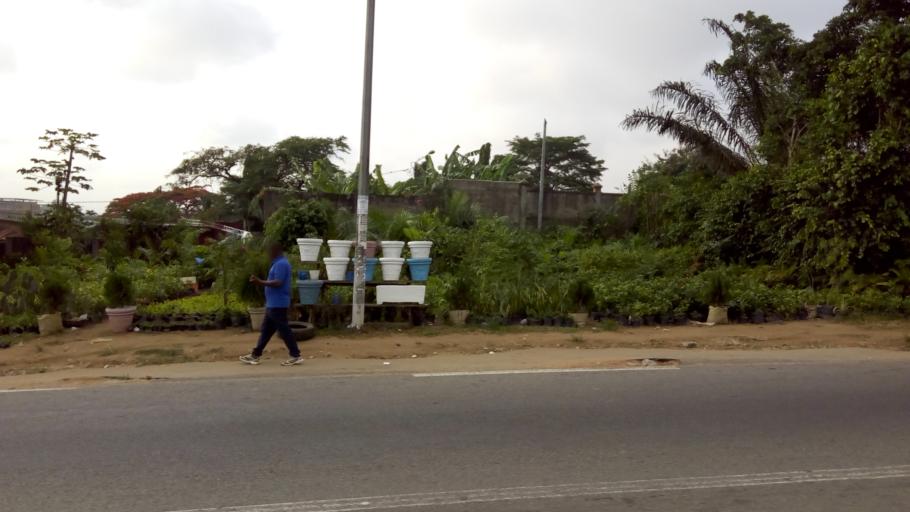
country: CI
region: Lagunes
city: Abidjan
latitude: 5.3486
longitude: -4.0004
